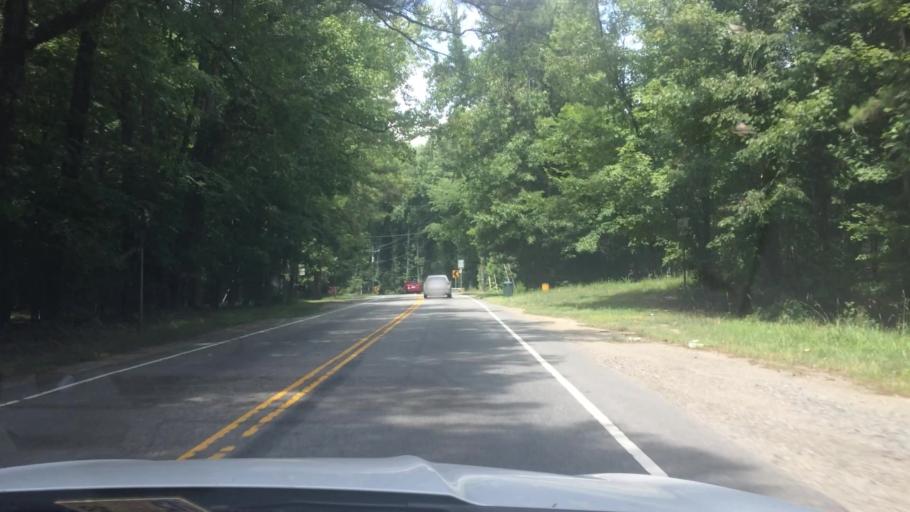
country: US
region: Virginia
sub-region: York County
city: Yorktown
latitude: 37.2087
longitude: -76.5876
